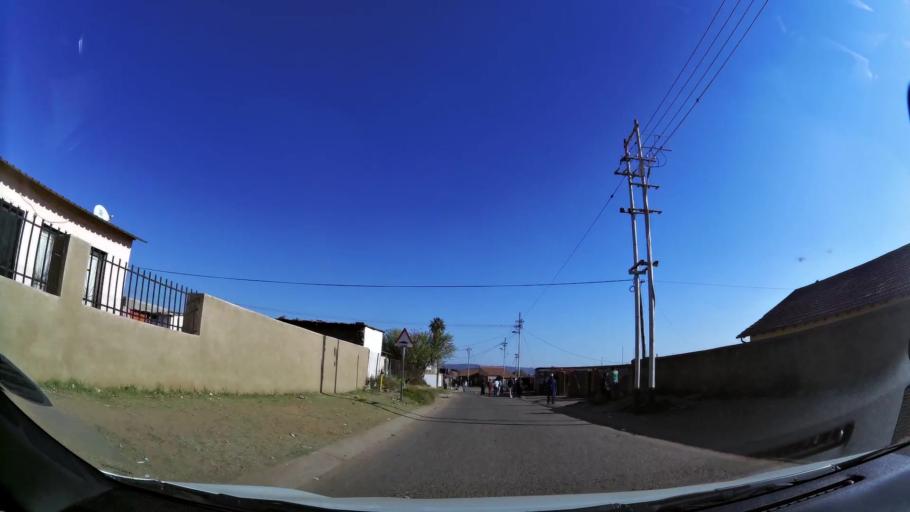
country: ZA
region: Gauteng
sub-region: City of Tshwane Metropolitan Municipality
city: Cullinan
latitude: -25.7162
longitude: 28.3817
